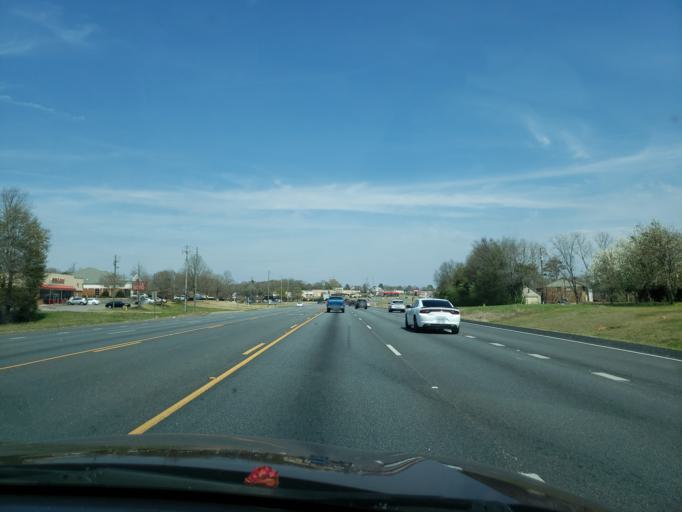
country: US
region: Alabama
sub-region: Elmore County
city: Millbrook
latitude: 32.5117
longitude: -86.3803
